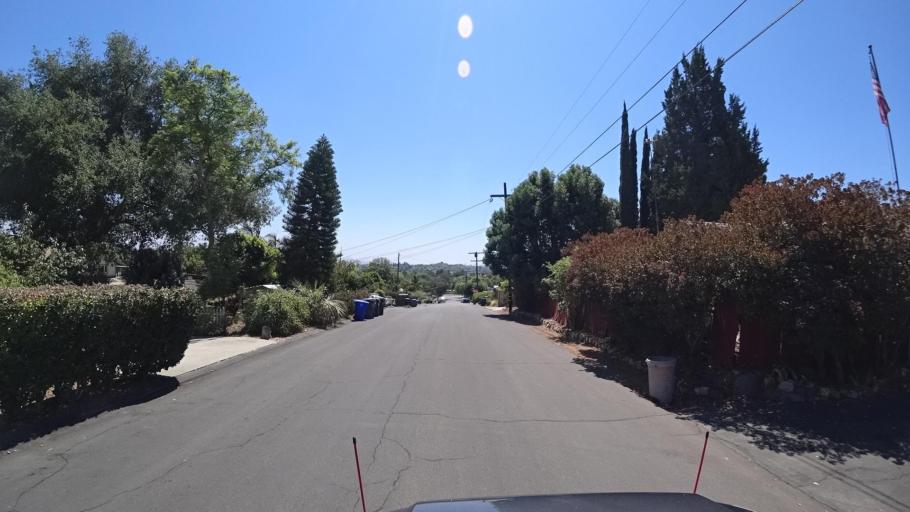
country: US
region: California
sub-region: San Diego County
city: Fallbrook
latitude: 33.3820
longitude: -117.2558
